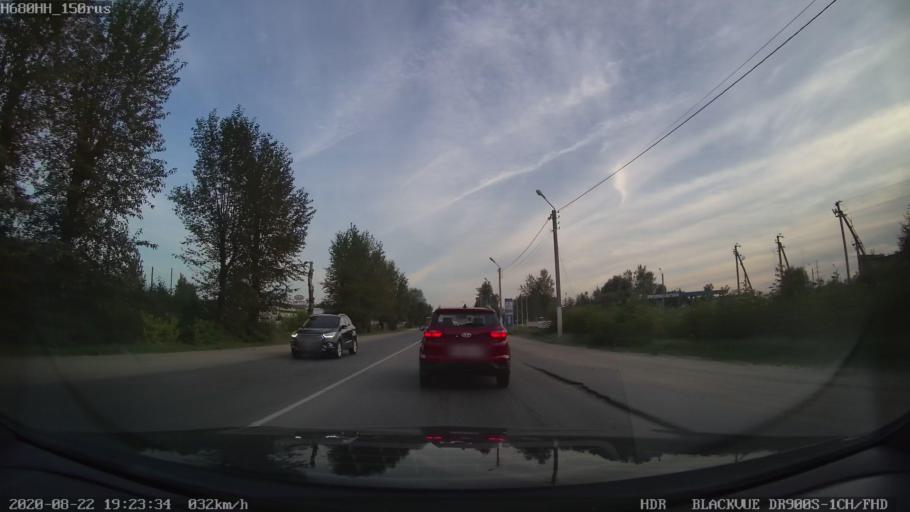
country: RU
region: Tverskaya
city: Tver
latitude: 56.8926
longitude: 35.9301
